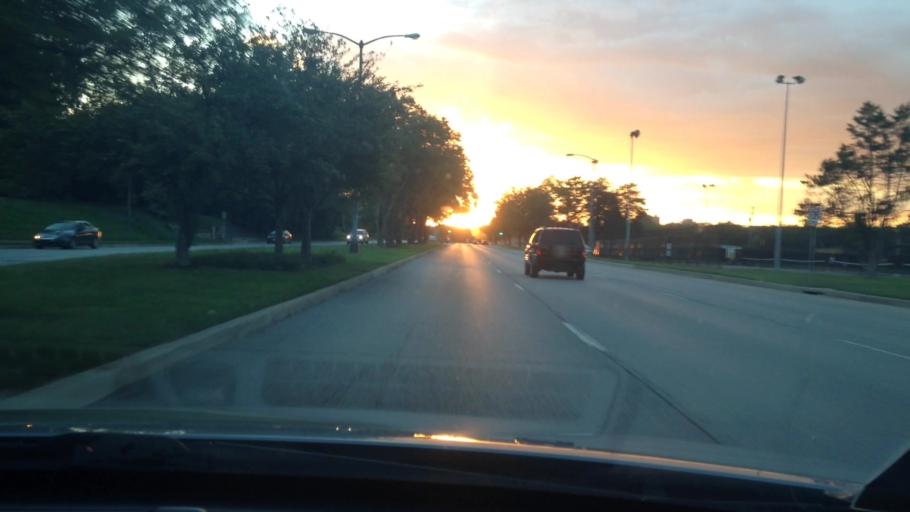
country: US
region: Kansas
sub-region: Johnson County
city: Westwood
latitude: 39.0410
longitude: -94.5610
